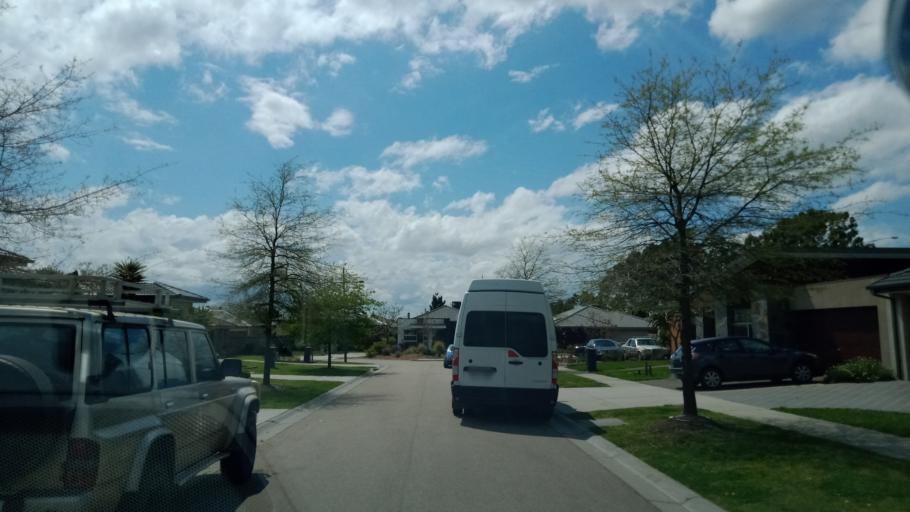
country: AU
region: Victoria
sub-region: Frankston
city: Sandhurst
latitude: -38.0830
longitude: 145.2004
